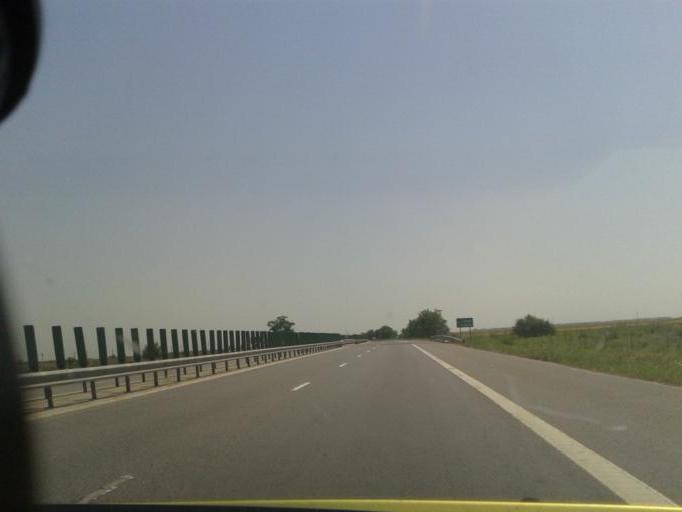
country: RO
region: Calarasi
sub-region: Comuna Nicolae Balcescu
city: Nicolae Balcescu
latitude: 44.4419
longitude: 26.7563
